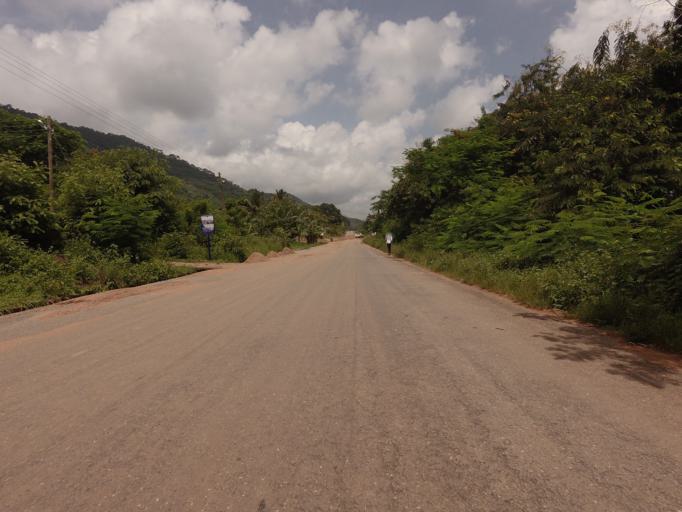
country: GH
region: Volta
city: Ho
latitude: 6.7361
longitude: 0.3478
